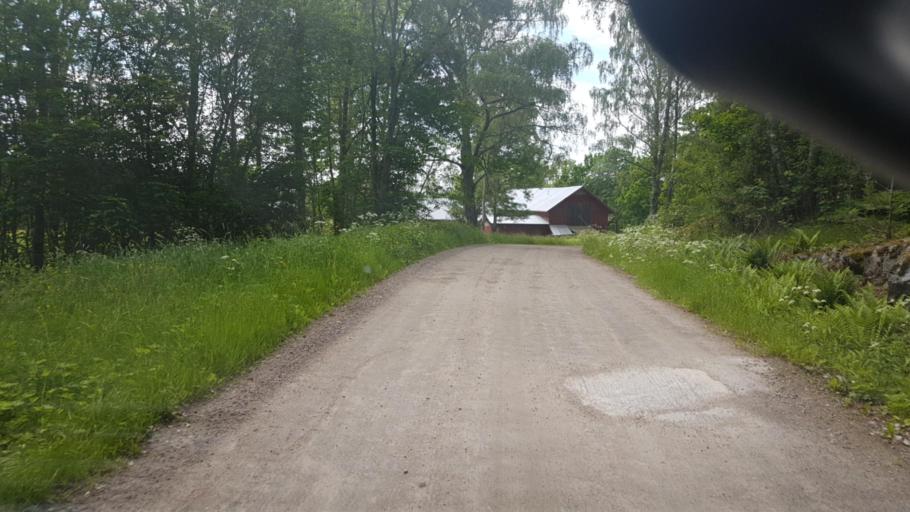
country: SE
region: Vaermland
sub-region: Eda Kommun
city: Amotfors
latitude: 59.7944
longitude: 12.4455
